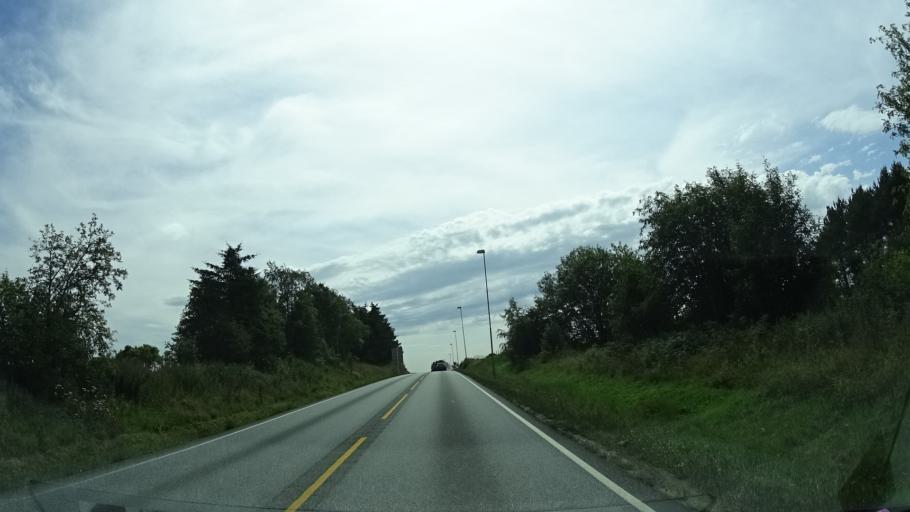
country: NO
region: Rogaland
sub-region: Randaberg
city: Randaberg
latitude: 59.0041
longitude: 5.6431
